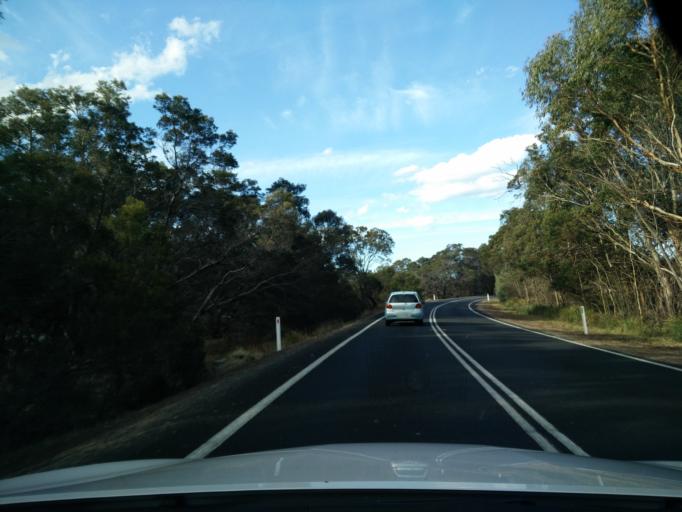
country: AU
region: Tasmania
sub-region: Break O'Day
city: St Helens
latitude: -42.0119
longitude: 148.2335
